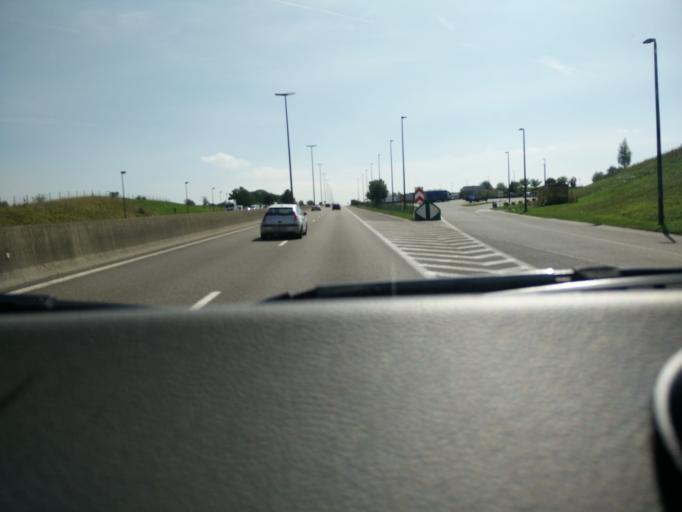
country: BE
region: Wallonia
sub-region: Province du Luxembourg
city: Habay-la-Vieille
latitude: 49.7149
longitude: 5.6026
